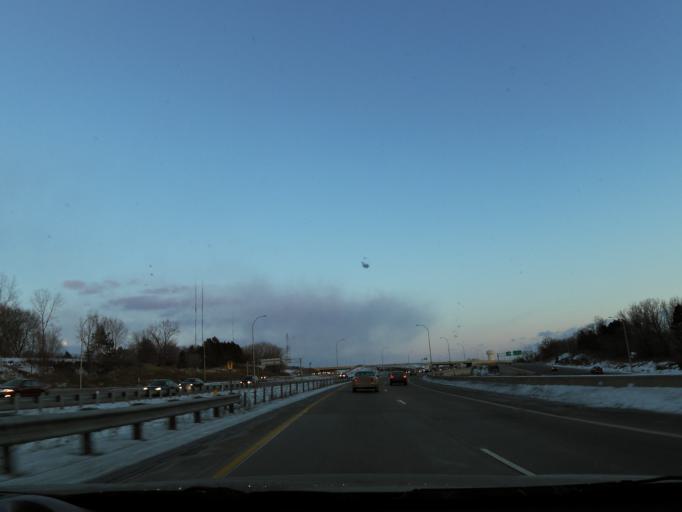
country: US
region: Minnesota
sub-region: Ramsey County
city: Arden Hills
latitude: 45.0660
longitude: -93.1654
